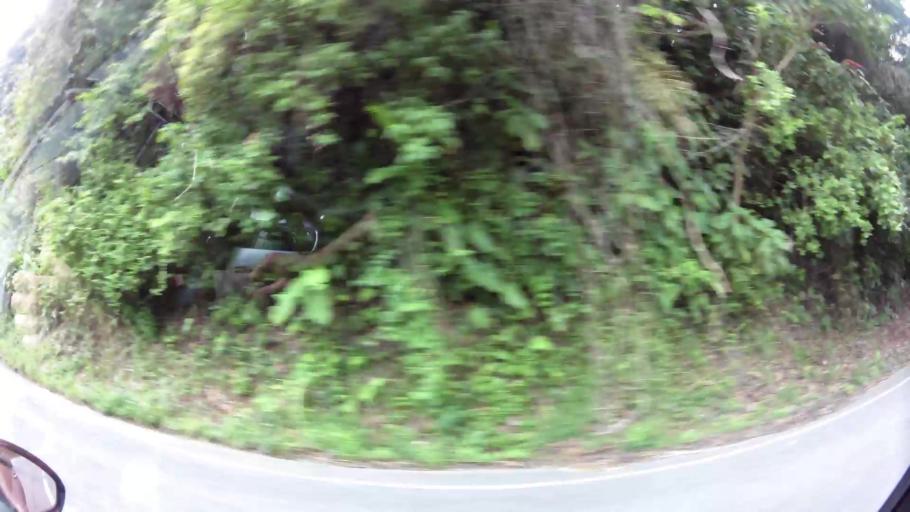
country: TT
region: Diego Martin
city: Petit Valley
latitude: 10.7591
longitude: -61.4451
